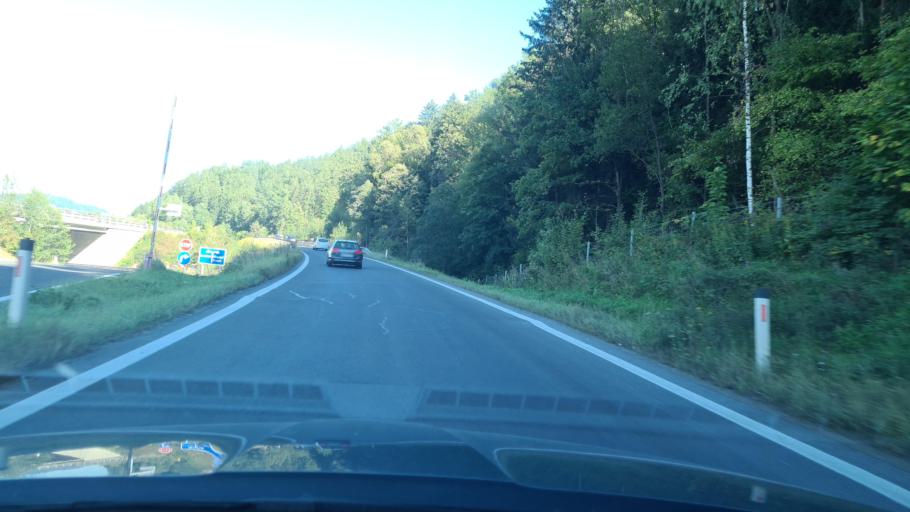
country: AT
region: Styria
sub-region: Politischer Bezirk Leoben
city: Proleb
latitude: 47.3828
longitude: 15.1272
